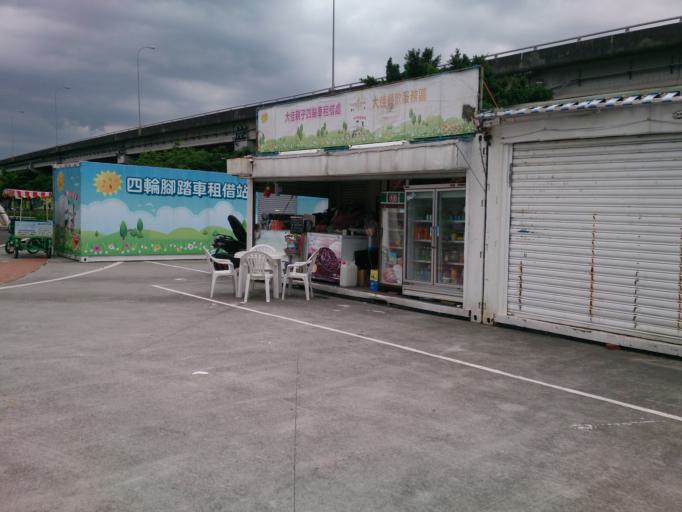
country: TW
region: Taipei
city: Taipei
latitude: 25.0740
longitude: 121.5392
